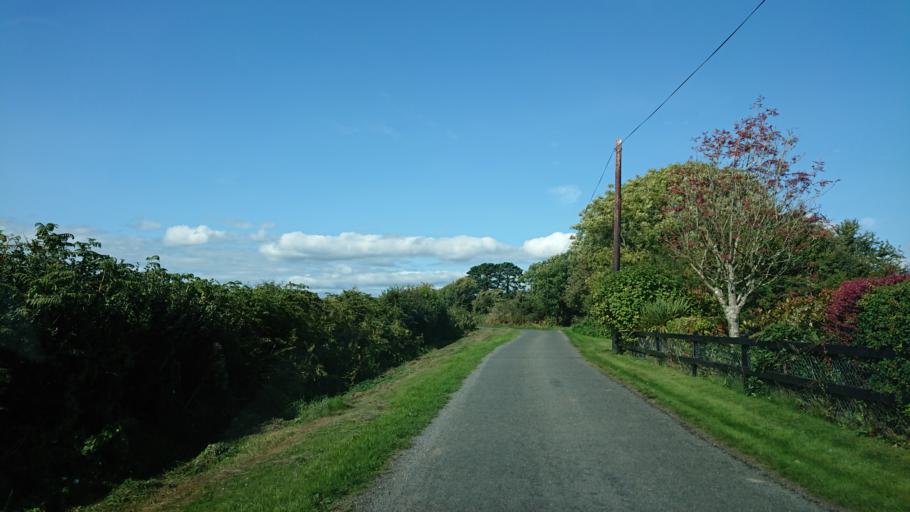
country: IE
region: Munster
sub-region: Waterford
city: Waterford
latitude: 52.2154
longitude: -7.0538
